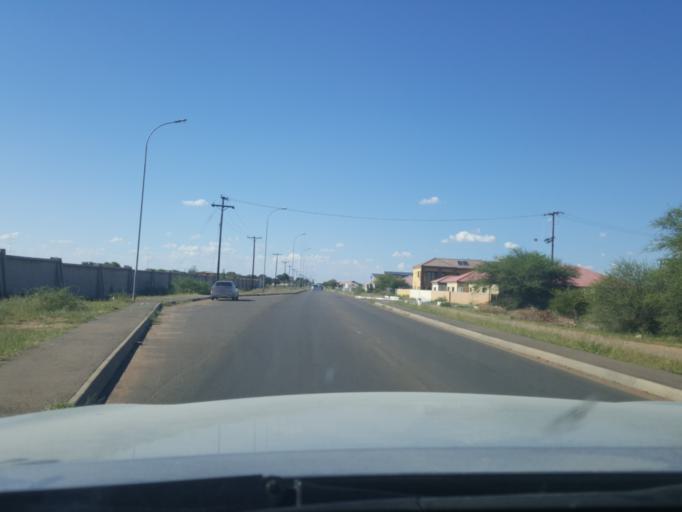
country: BW
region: South East
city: Gaborone
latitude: -24.6169
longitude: 25.9469
